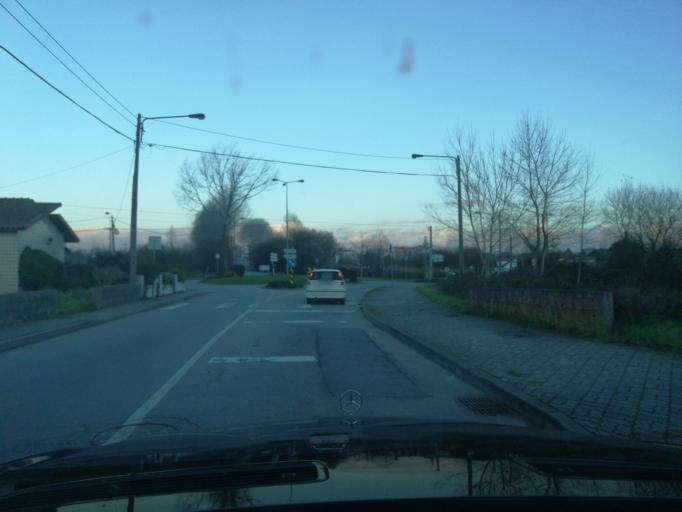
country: PT
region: Aveiro
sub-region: Estarreja
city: Estarreja
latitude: 40.7558
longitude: -8.5813
